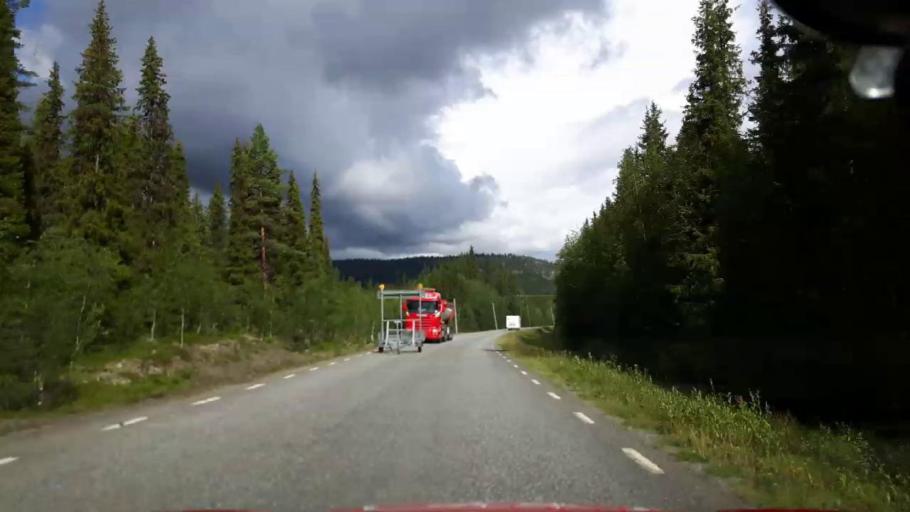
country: SE
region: Vaesterbotten
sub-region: Vilhelmina Kommun
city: Sjoberg
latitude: 64.9324
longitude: 15.8591
